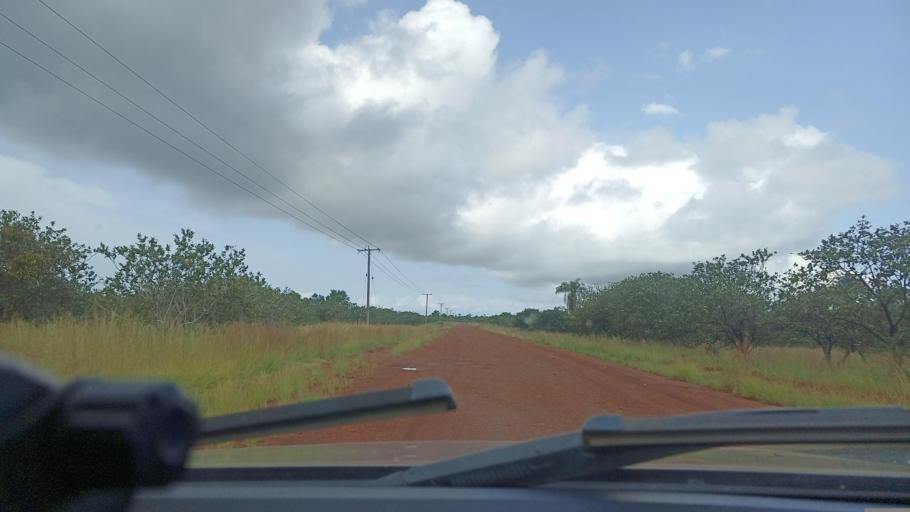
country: LR
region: Grand Cape Mount
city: Robertsport
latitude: 6.6917
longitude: -11.2745
